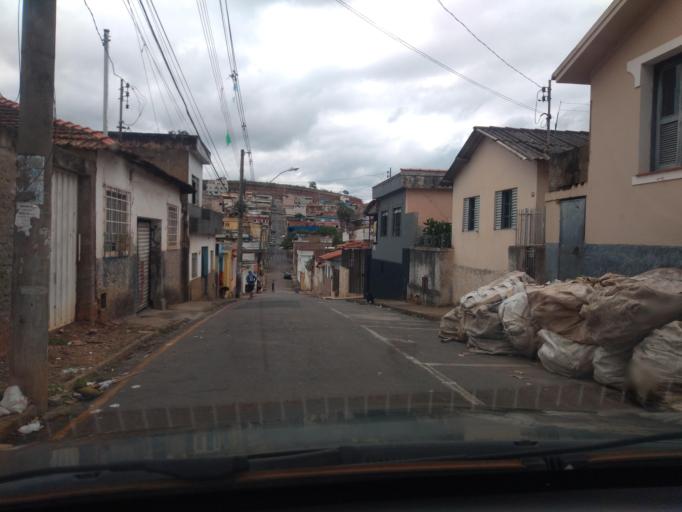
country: BR
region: Minas Gerais
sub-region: Tres Coracoes
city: Tres Coracoes
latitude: -21.6927
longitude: -45.2558
